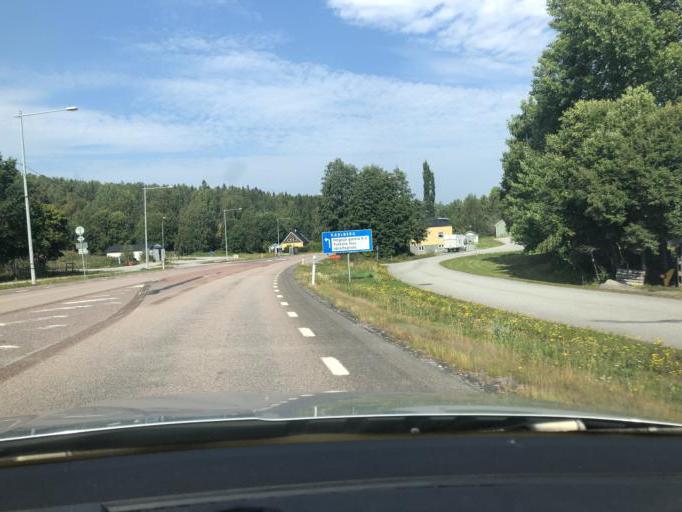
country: SE
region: Vaesternorrland
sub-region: Kramfors Kommun
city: Kramfors
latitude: 62.8038
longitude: 17.8674
